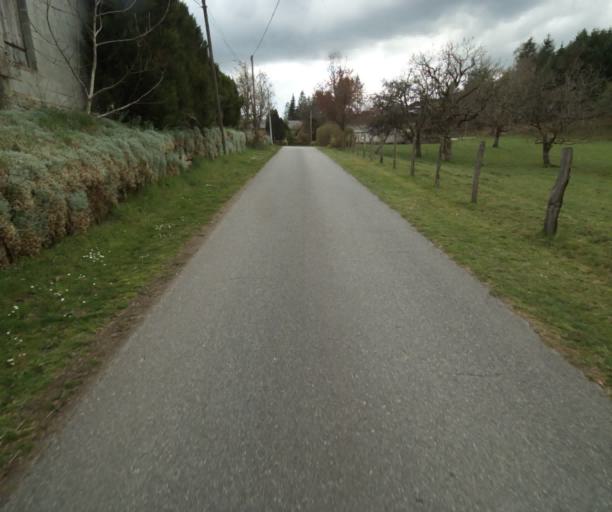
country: FR
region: Limousin
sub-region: Departement de la Correze
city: Correze
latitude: 45.3045
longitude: 1.9313
